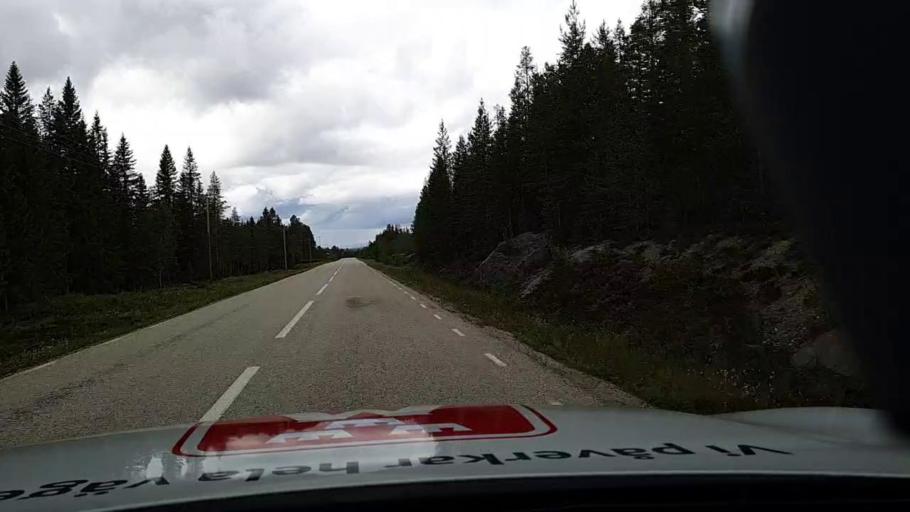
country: SE
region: Jaemtland
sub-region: Are Kommun
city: Jarpen
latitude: 62.7705
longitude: 13.7166
